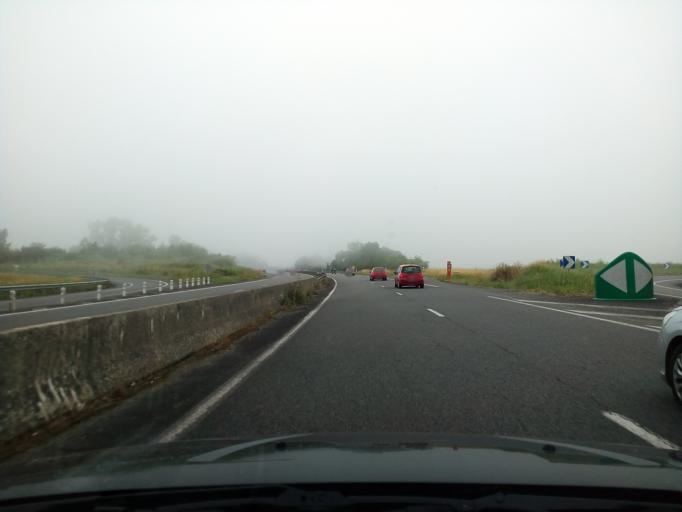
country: FR
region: Poitou-Charentes
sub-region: Departement de la Charente
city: Jarnac
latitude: 45.6924
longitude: -0.1364
